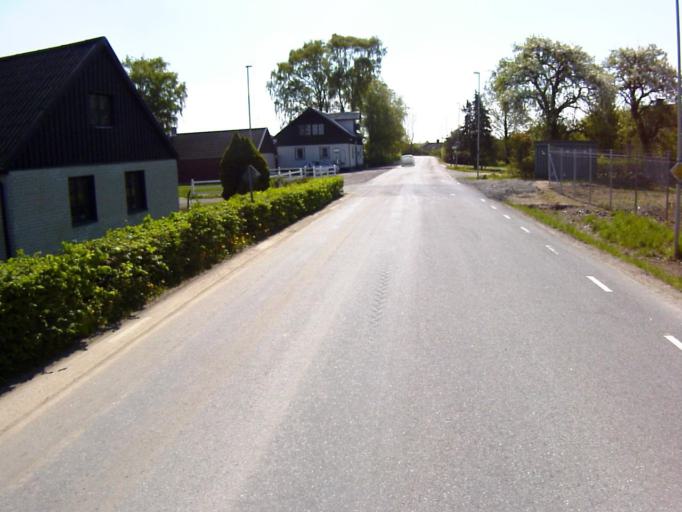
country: SE
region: Skane
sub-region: Kristianstads Kommun
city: Kristianstad
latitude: 56.0224
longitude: 14.2137
